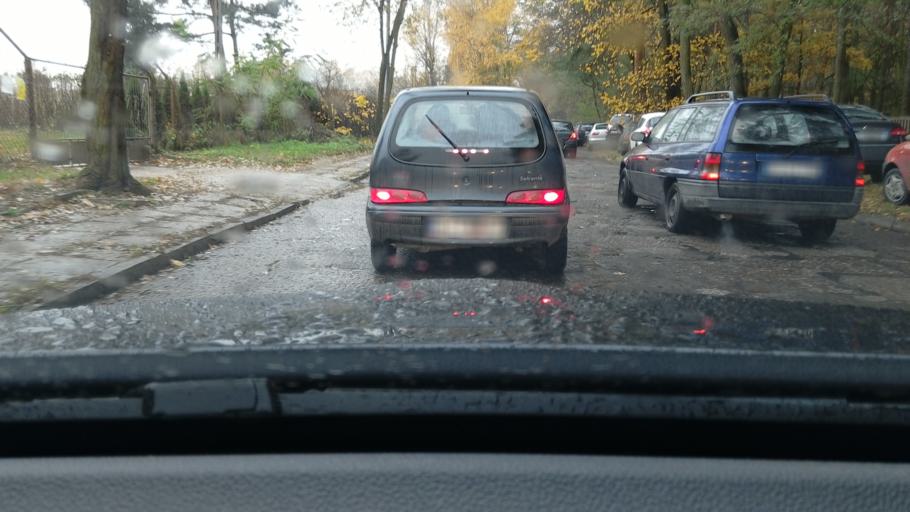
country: PL
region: Lodz Voivodeship
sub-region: Skierniewice
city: Skierniewice
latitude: 51.9366
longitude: 20.1576
